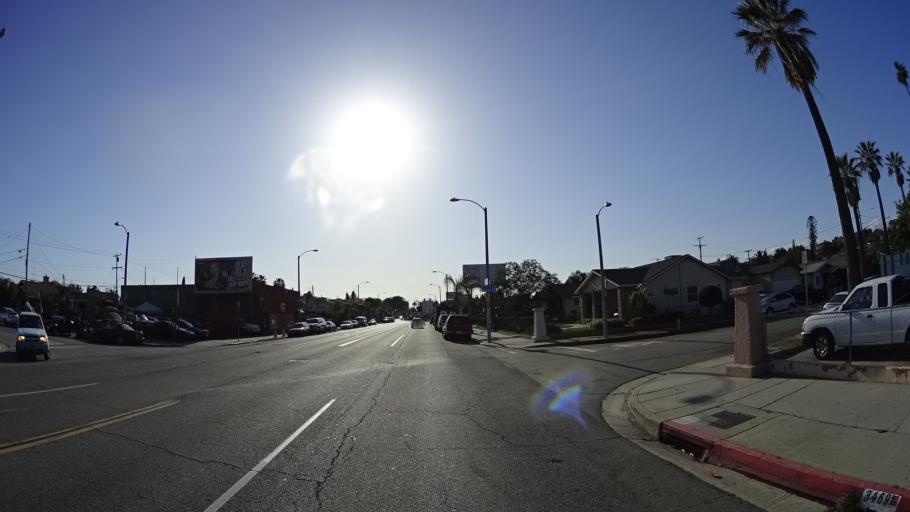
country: US
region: California
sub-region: Los Angeles County
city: Boyle Heights
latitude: 34.0405
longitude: -118.1899
